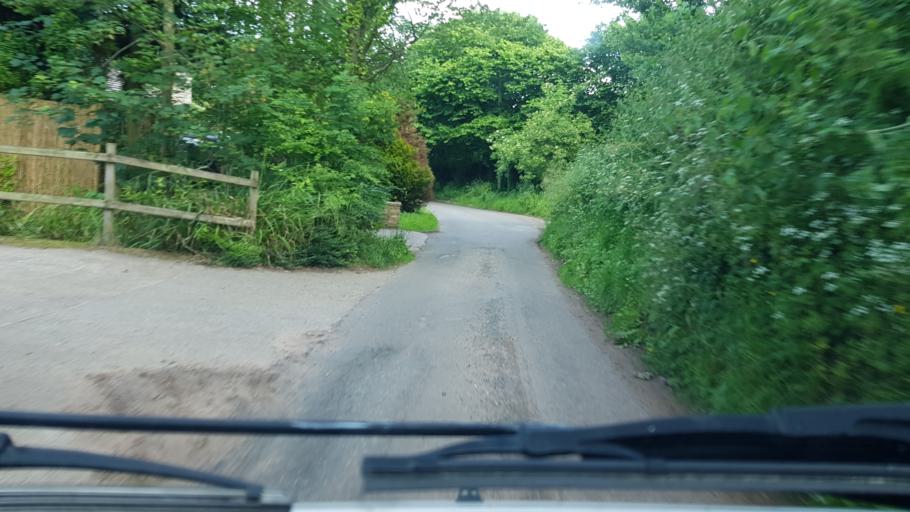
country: GB
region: England
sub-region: Worcestershire
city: Bewdley
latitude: 52.3268
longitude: -2.3114
